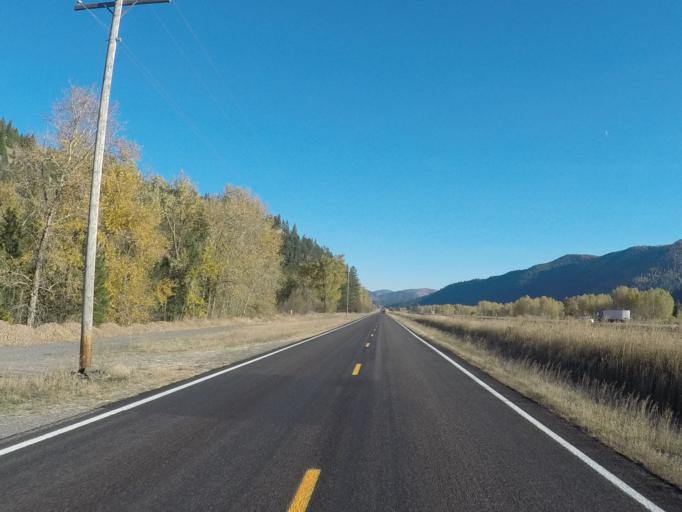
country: US
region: Montana
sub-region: Missoula County
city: Clinton
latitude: 46.8183
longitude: -113.7973
